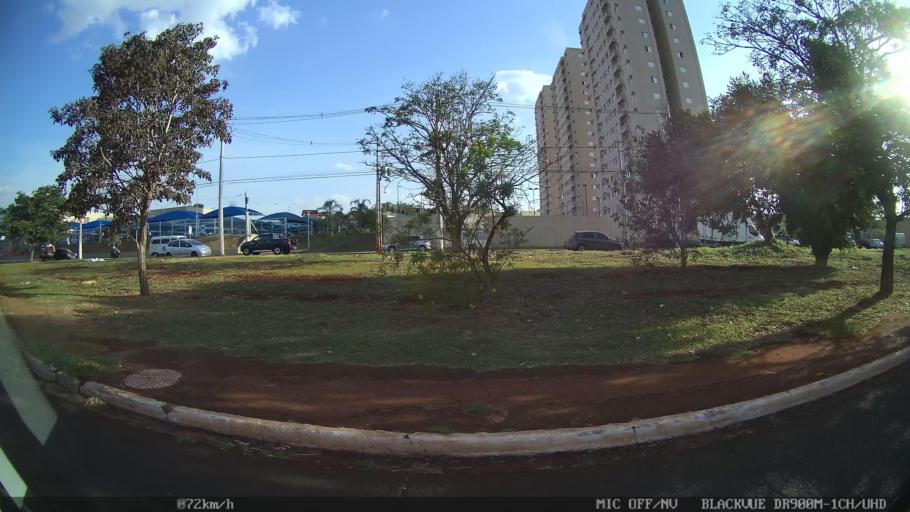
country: BR
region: Sao Paulo
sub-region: Ribeirao Preto
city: Ribeirao Preto
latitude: -21.1356
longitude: -47.8373
